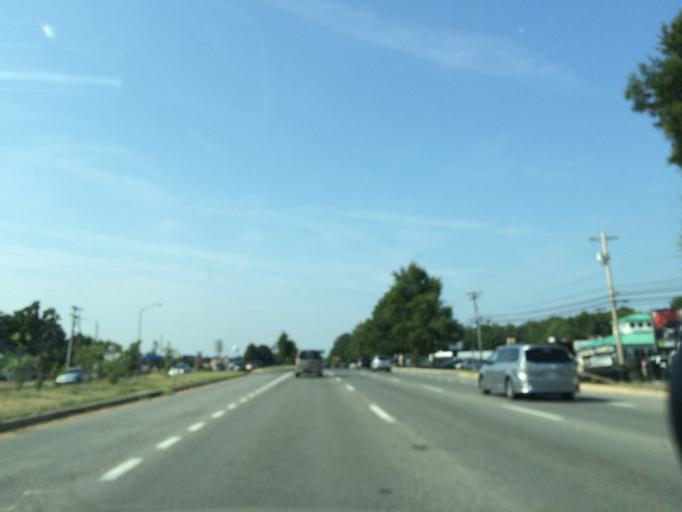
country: US
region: Maryland
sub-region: Charles County
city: Waldorf
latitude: 38.6334
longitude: -76.9036
